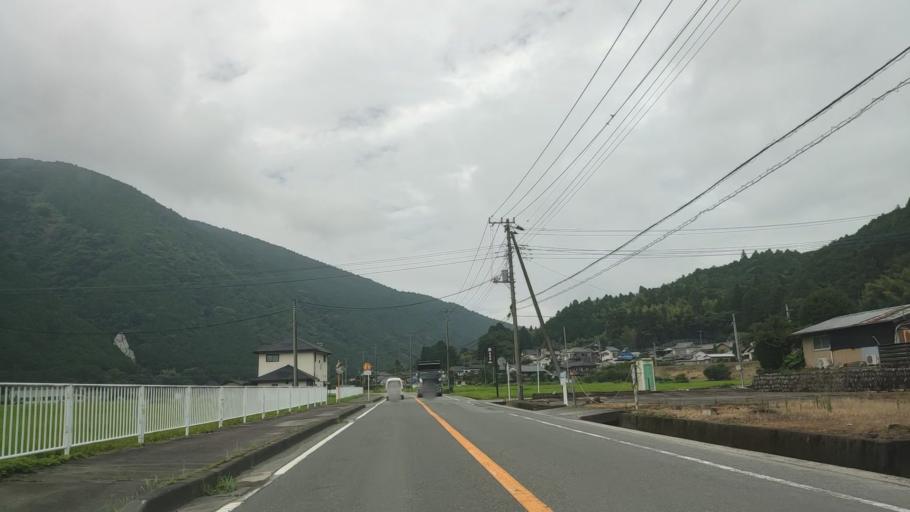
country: JP
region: Shizuoka
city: Fujinomiya
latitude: 35.2102
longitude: 138.5491
